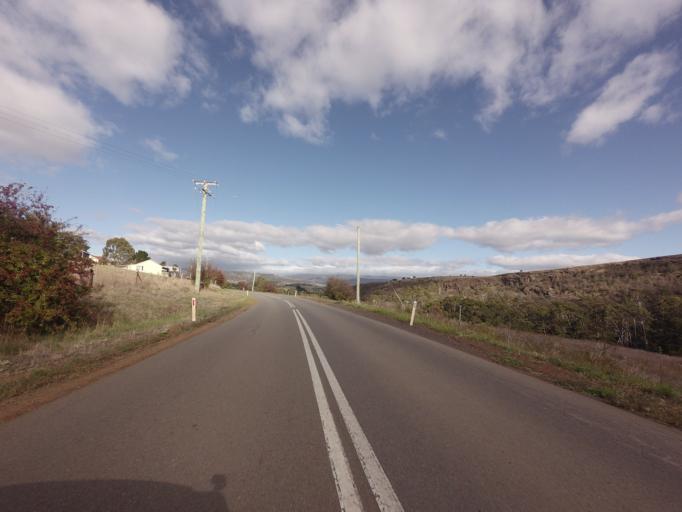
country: AU
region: Tasmania
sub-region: Derwent Valley
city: New Norfolk
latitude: -42.6980
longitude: 146.9210
